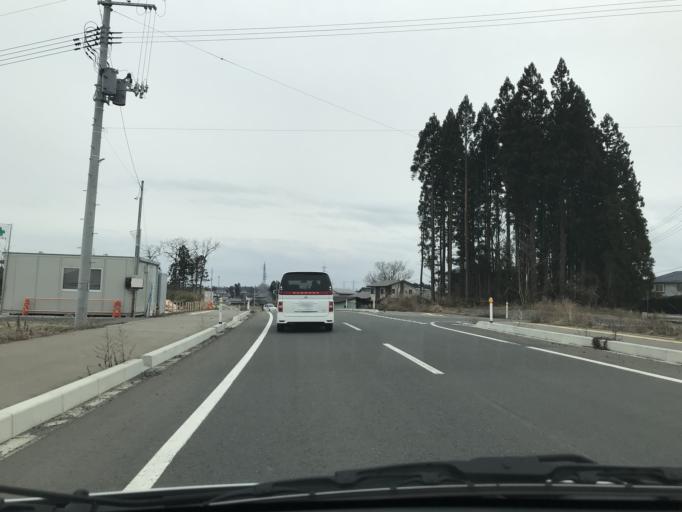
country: JP
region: Iwate
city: Hanamaki
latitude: 39.3507
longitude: 141.1031
